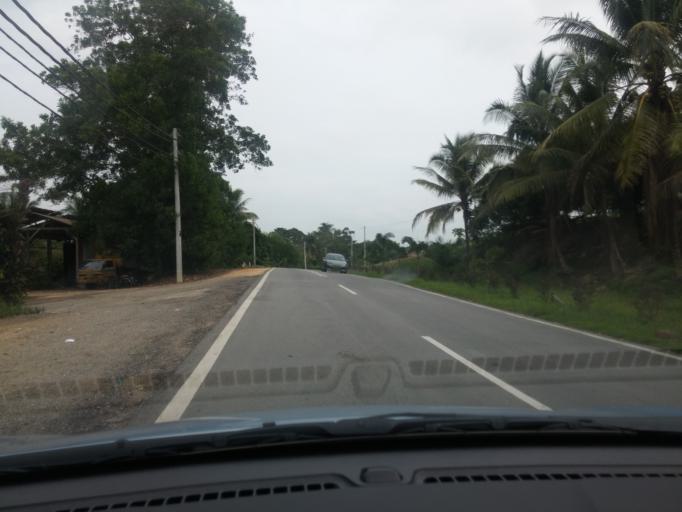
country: MY
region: Pahang
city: Kuantan
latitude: 3.8381
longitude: 103.1616
